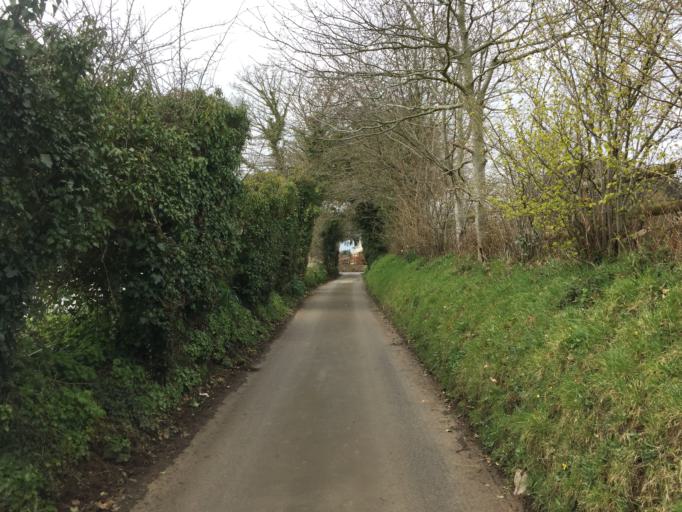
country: JE
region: St Helier
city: Saint Helier
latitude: 49.2151
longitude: -2.1399
